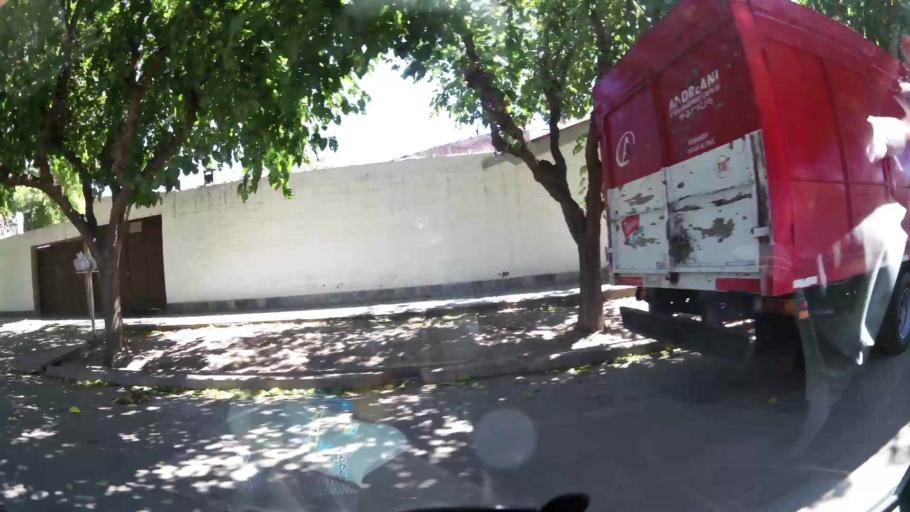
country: AR
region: Mendoza
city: Las Heras
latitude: -32.8507
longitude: -68.8491
